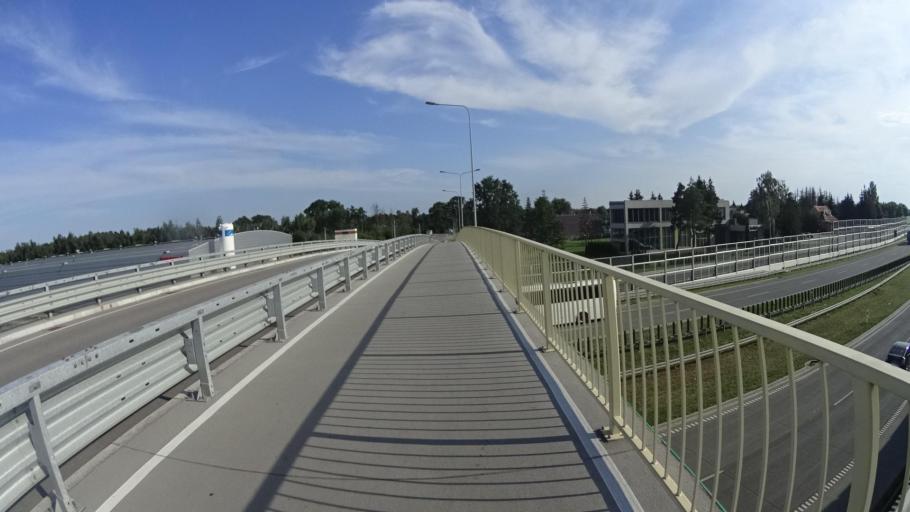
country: PL
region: Masovian Voivodeship
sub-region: Powiat pruszkowski
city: Nadarzyn
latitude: 52.0831
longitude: 20.7944
